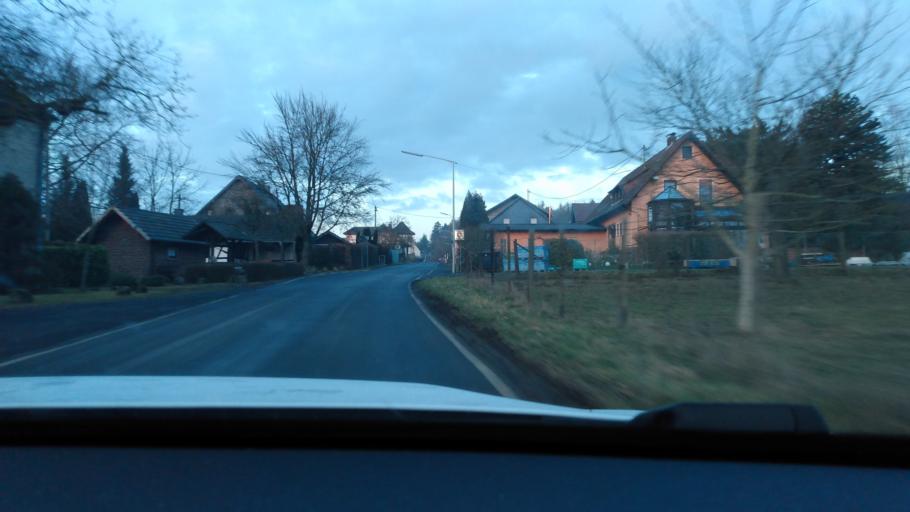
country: DE
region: Rheinland-Pfalz
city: Kircheib
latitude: 50.7054
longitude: 7.4678
